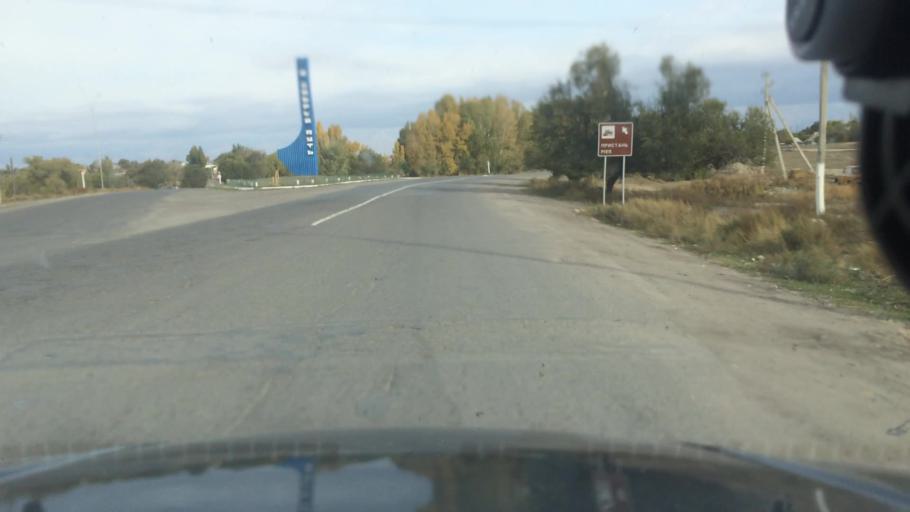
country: KG
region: Ysyk-Koel
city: Karakol
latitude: 42.5322
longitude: 78.3828
